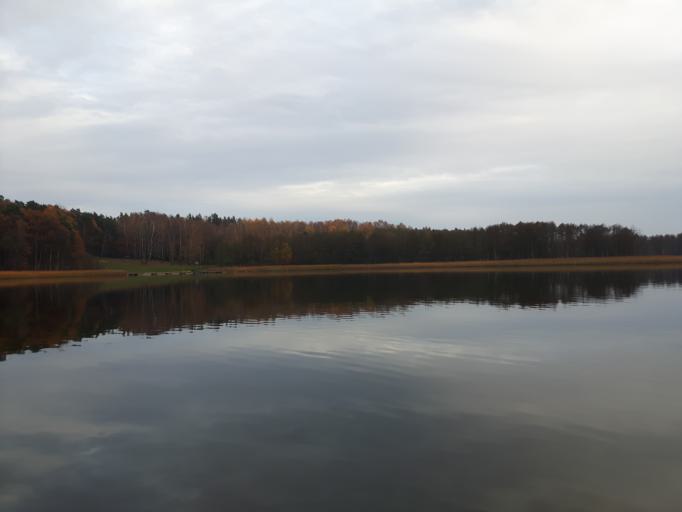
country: PL
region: Warmian-Masurian Voivodeship
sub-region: Powiat olsztynski
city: Barczewo
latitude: 53.8278
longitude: 20.7371
